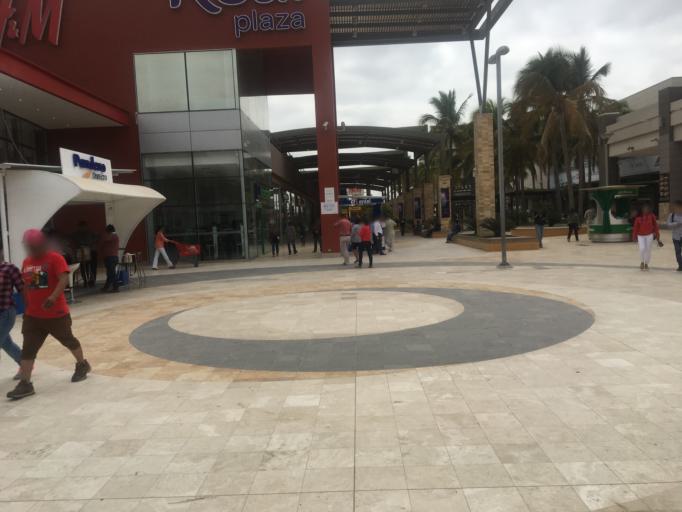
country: PE
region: Piura
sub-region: Provincia de Piura
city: Piura
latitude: -5.1864
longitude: -80.6426
